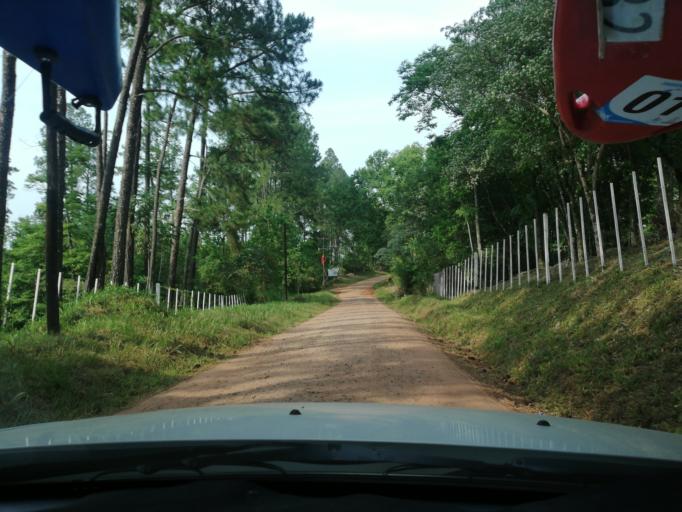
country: AR
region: Misiones
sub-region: Departamento de San Ignacio
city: San Ignacio
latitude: -27.2922
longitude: -55.5636
